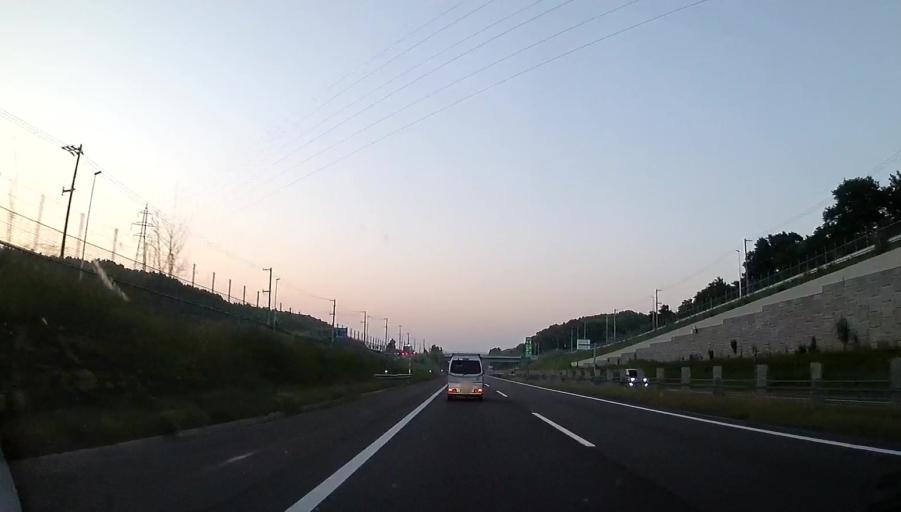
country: JP
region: Hokkaido
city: Kitahiroshima
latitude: 42.9993
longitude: 141.4680
